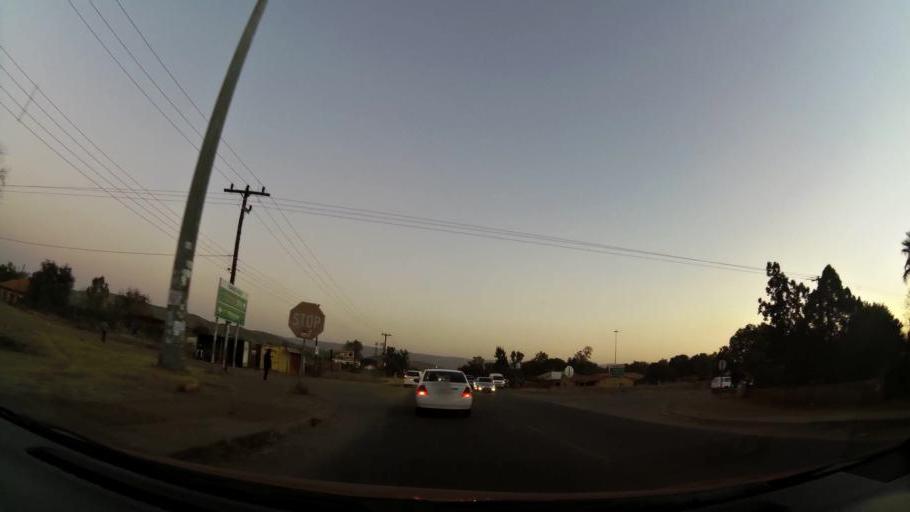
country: ZA
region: North-West
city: Ga-Rankuwa
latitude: -25.6142
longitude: 27.9634
